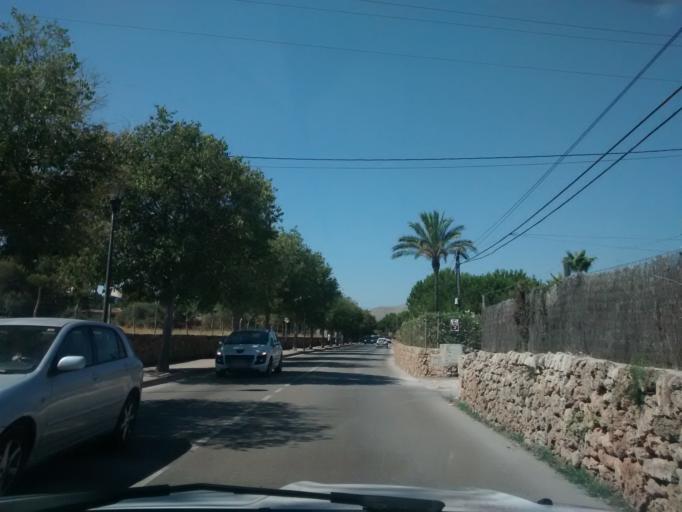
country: ES
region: Balearic Islands
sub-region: Illes Balears
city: Alcudia
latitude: 39.8583
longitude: 3.1365
